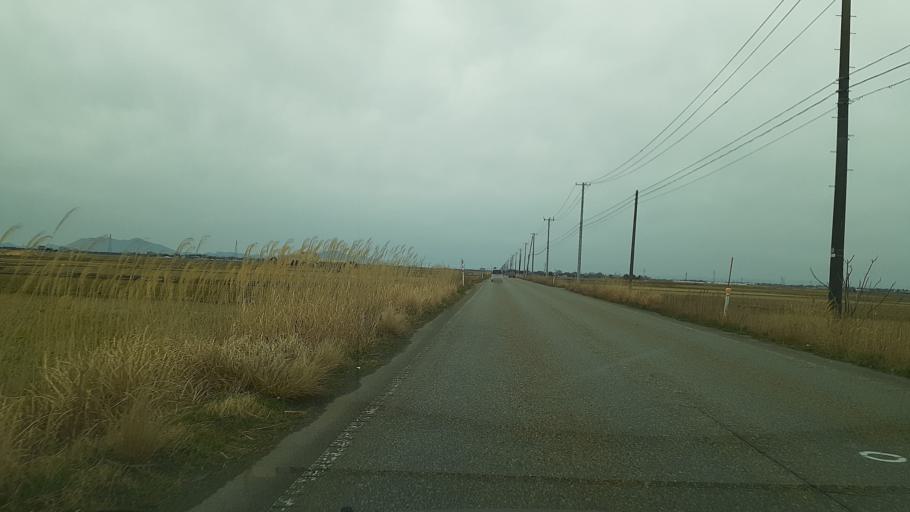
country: JP
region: Niigata
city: Niitsu-honcho
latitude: 37.8157
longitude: 139.0938
